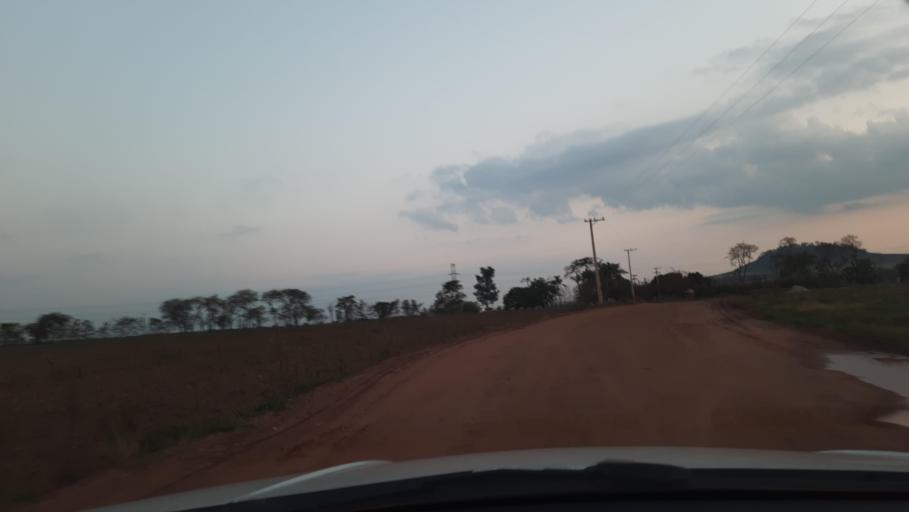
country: BR
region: Sao Paulo
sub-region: Santa Cruz Das Palmeiras
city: Santa Cruz das Palmeiras
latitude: -21.8046
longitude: -47.1819
